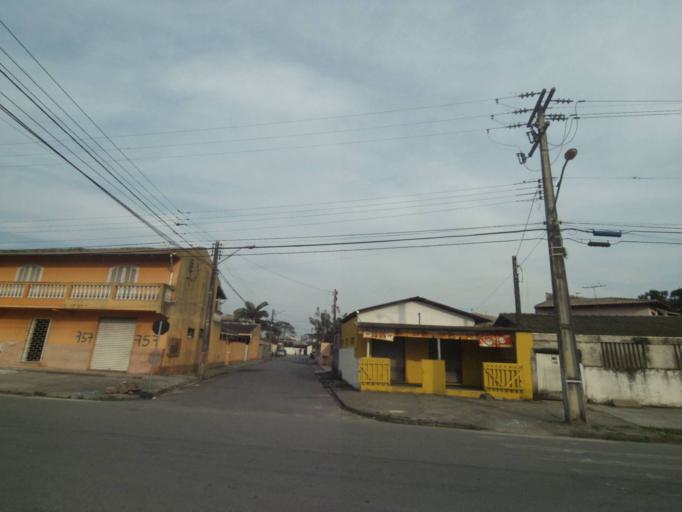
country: BR
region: Parana
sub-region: Paranagua
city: Paranagua
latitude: -25.5216
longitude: -48.5341
